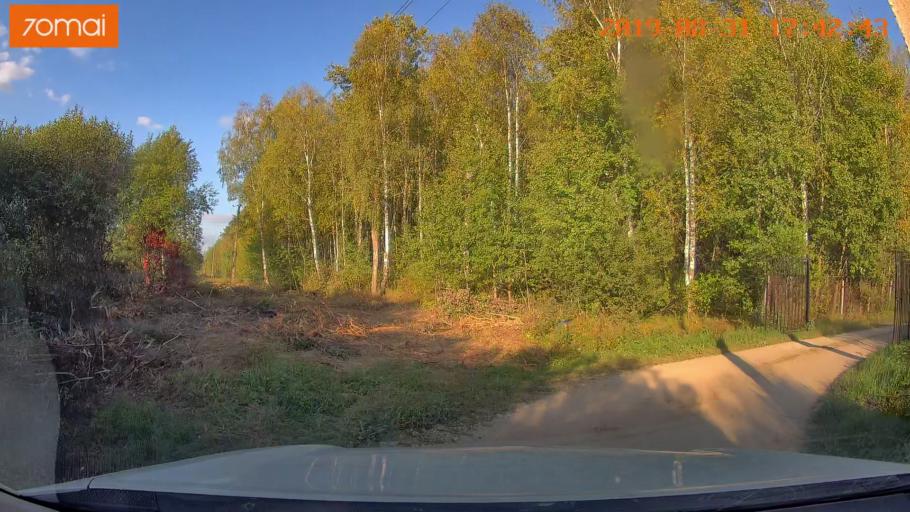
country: RU
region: Kaluga
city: Detchino
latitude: 54.8227
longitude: 36.3713
